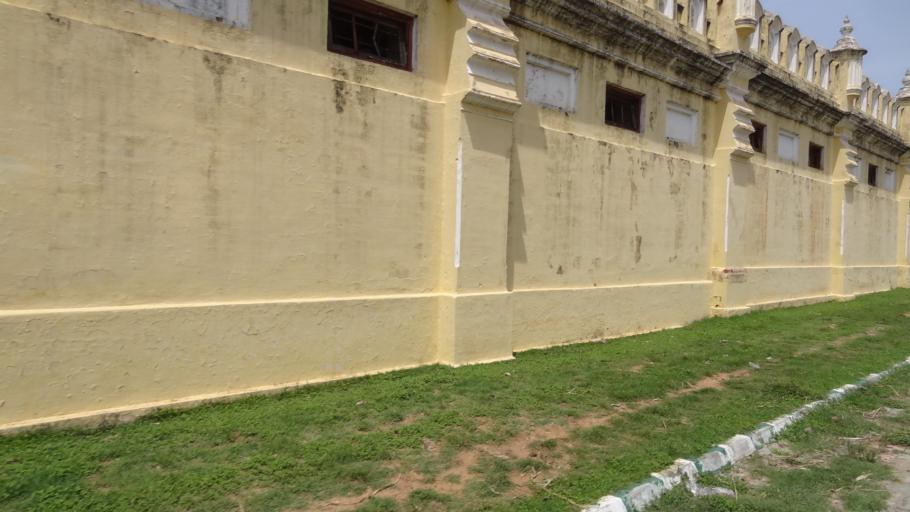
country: IN
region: Karnataka
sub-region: Mysore
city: Mysore
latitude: 12.3072
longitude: 76.6544
